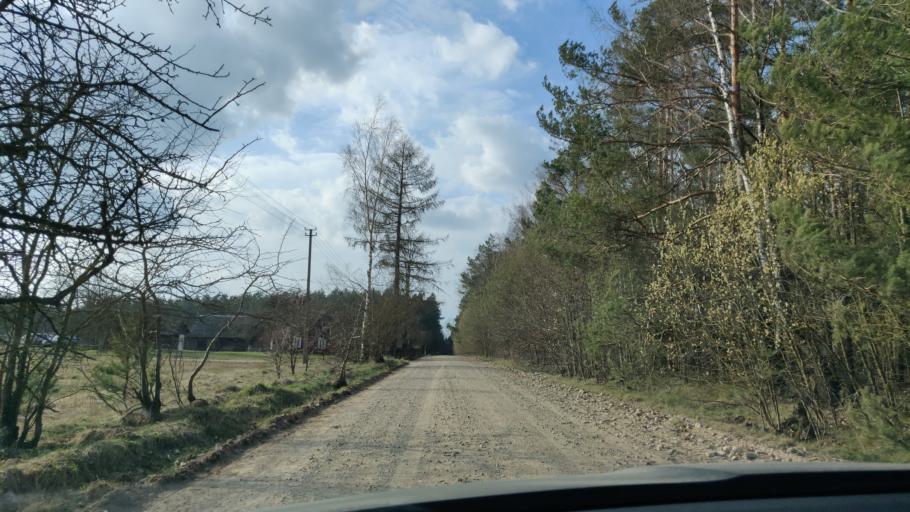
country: LT
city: Lentvaris
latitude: 54.5958
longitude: 25.0835
